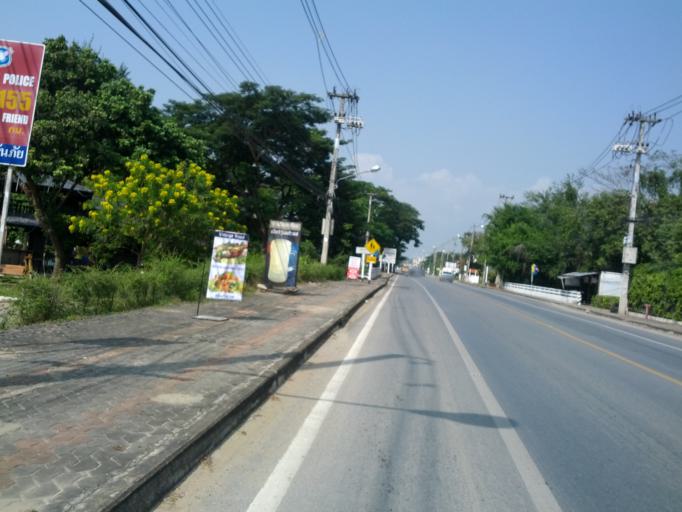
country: TH
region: Chiang Mai
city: Chiang Mai
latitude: 18.7795
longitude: 99.0463
